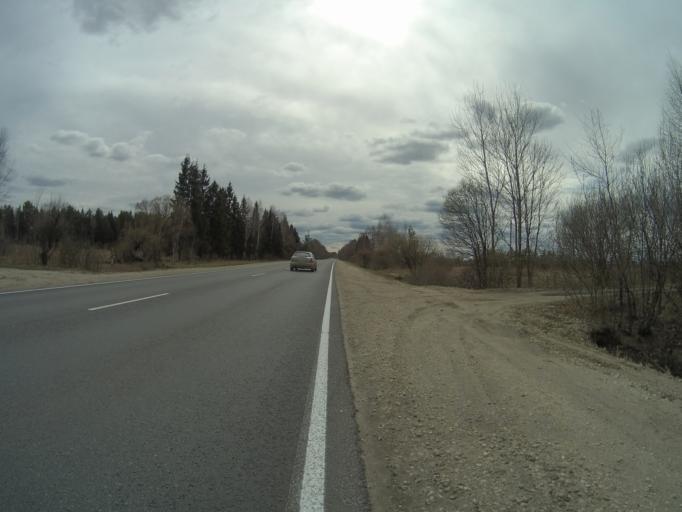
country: RU
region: Vladimir
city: Golovino
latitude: 56.0063
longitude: 40.5694
